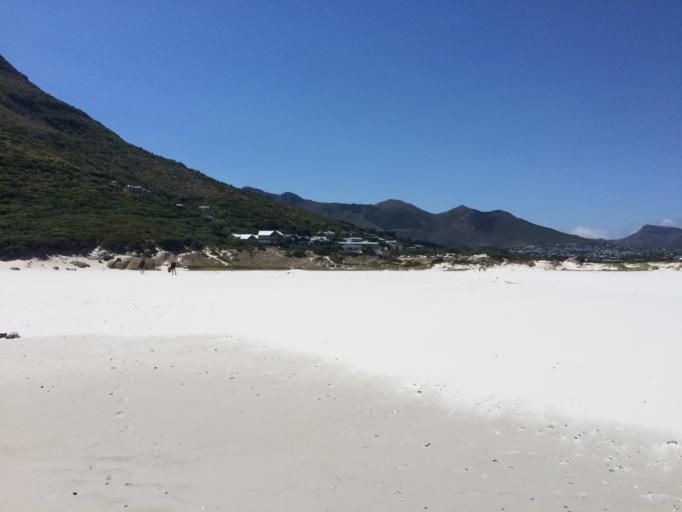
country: ZA
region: Western Cape
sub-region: City of Cape Town
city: Constantia
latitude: -34.0991
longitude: 18.3531
